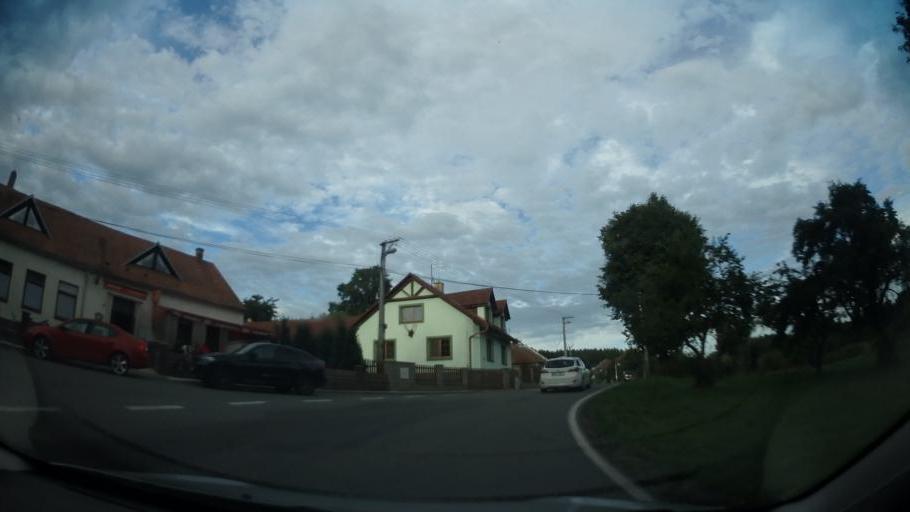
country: CZ
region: Olomoucky
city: Horni Stepanov
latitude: 49.5607
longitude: 16.7529
